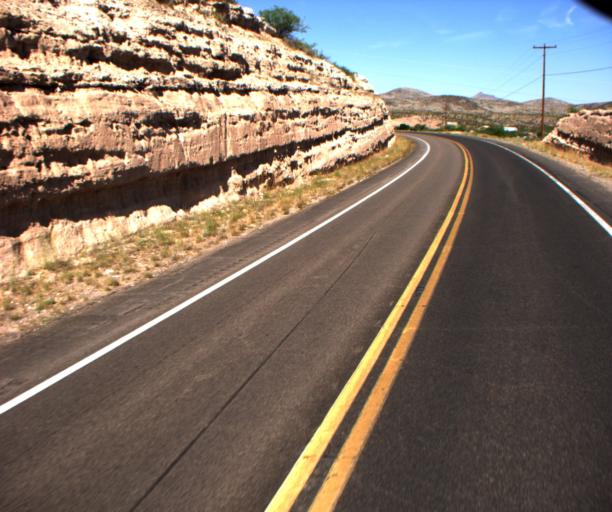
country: US
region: Arizona
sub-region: Greenlee County
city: Clifton
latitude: 32.7419
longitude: -109.1307
